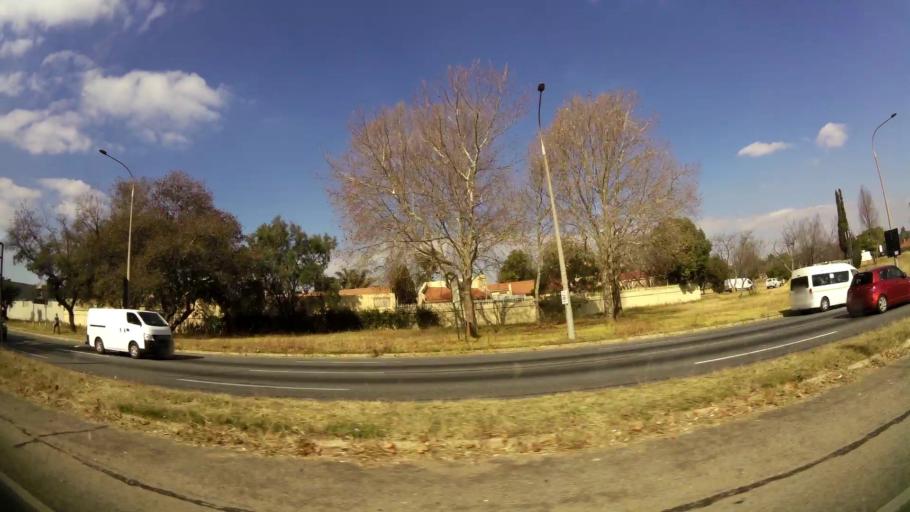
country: ZA
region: Gauteng
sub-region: West Rand District Municipality
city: Krugersdorp
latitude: -26.0872
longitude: 27.7856
